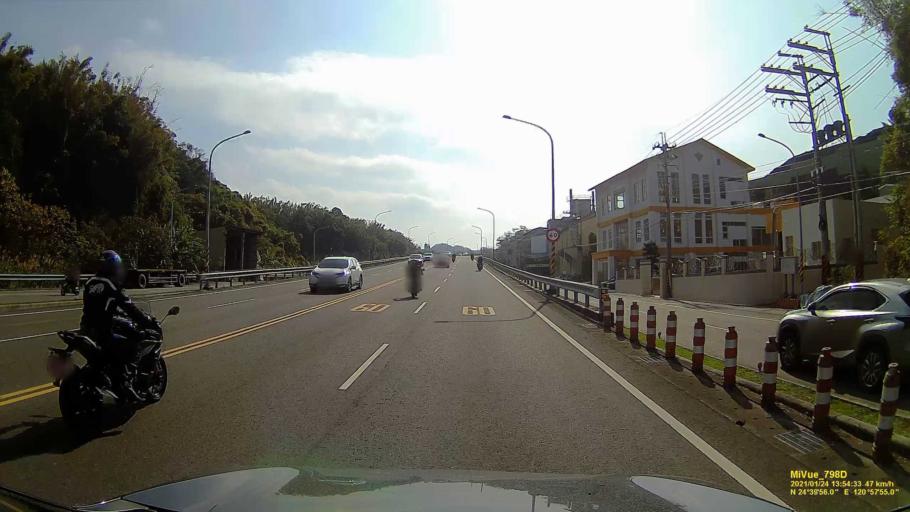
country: TW
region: Taiwan
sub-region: Hsinchu
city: Hsinchu
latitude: 24.6654
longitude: 120.9652
